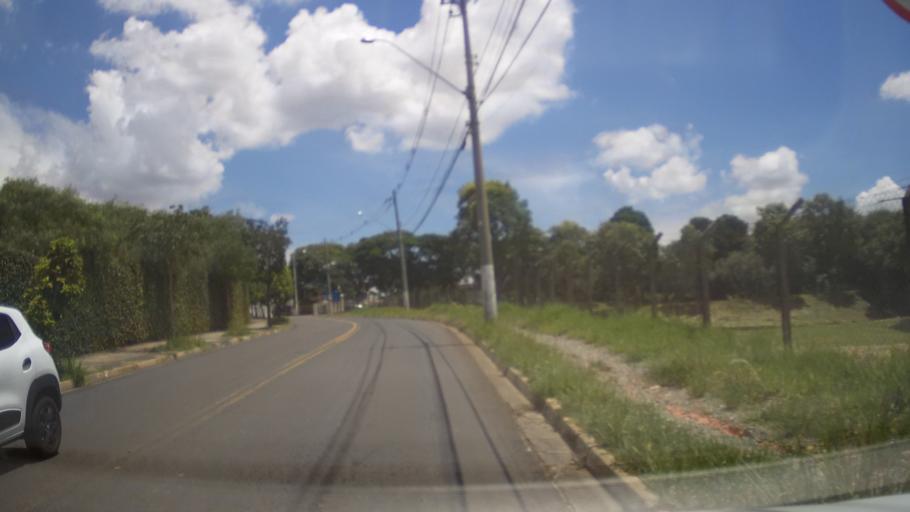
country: BR
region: Sao Paulo
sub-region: Valinhos
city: Valinhos
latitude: -22.9499
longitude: -46.9990
